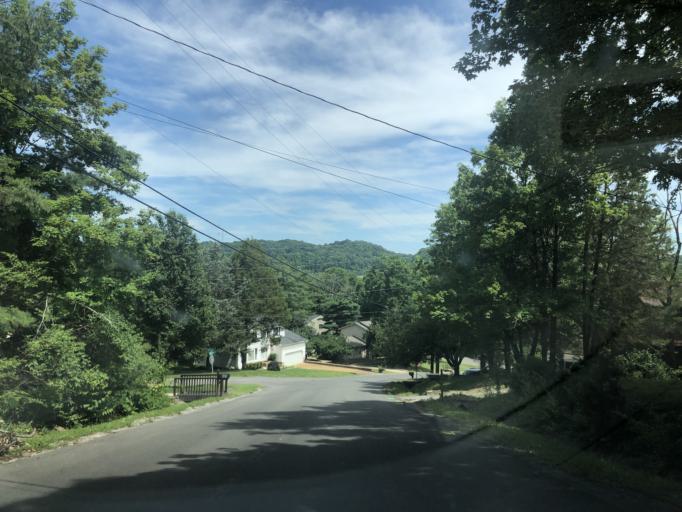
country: US
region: Tennessee
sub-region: Davidson County
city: Belle Meade
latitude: 36.0777
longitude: -86.9314
